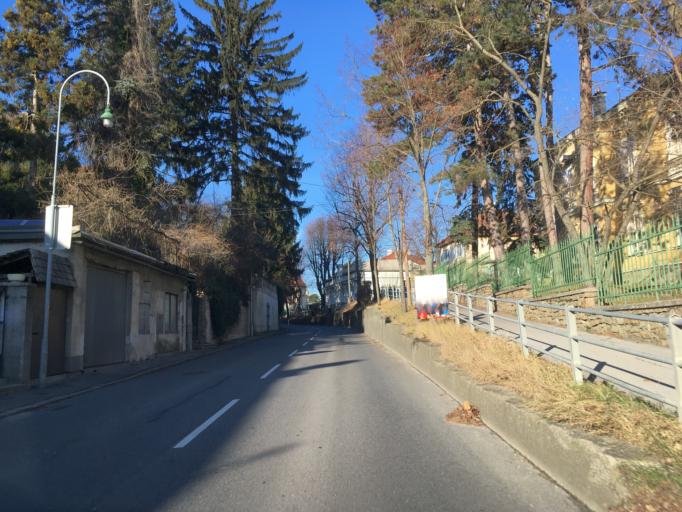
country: AT
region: Lower Austria
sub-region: Politischer Bezirk Wien-Umgebung
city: Klosterneuburg
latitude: 48.3264
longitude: 16.3032
